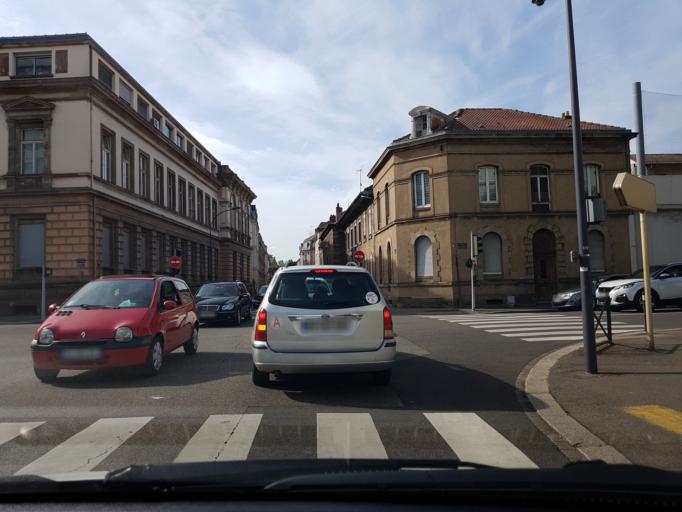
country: FR
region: Alsace
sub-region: Departement du Haut-Rhin
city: Mulhouse
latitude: 47.7523
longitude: 7.3430
